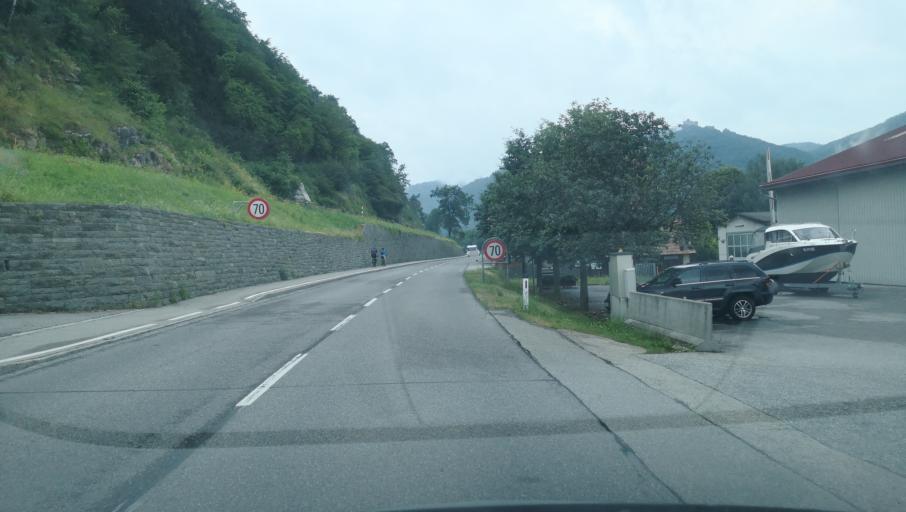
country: AT
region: Lower Austria
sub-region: Politischer Bezirk Krems
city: Aggsbach
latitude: 48.2997
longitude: 15.4046
